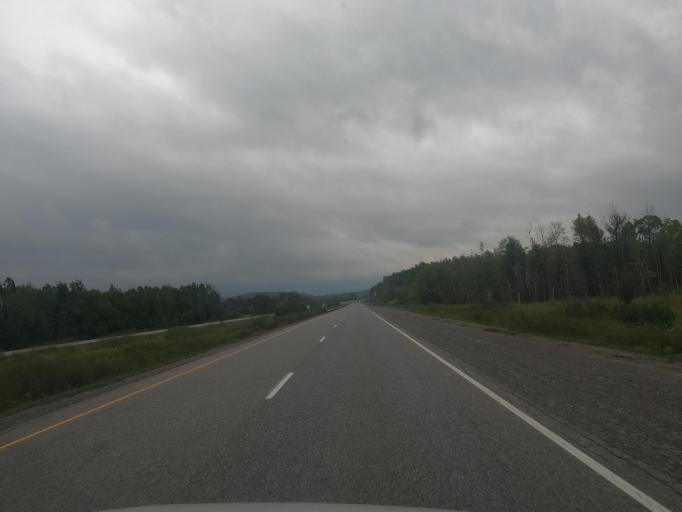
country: CA
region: Ontario
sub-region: Algoma
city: Sault Ste. Marie
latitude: 46.5099
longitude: -84.0501
